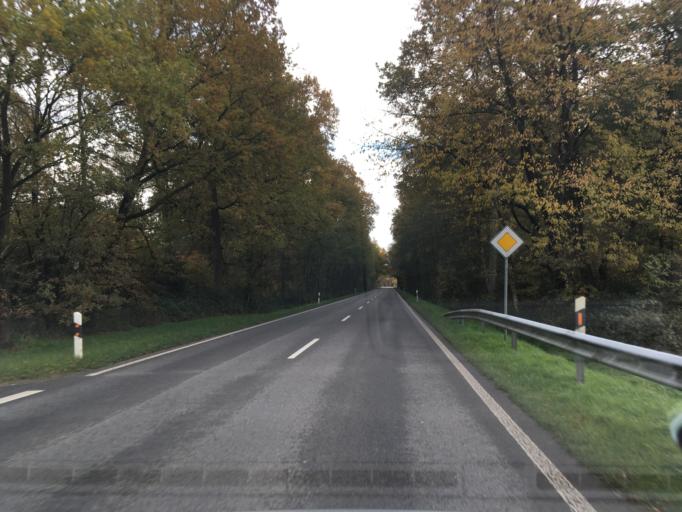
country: DE
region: North Rhine-Westphalia
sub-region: Regierungsbezirk Munster
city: Heiden
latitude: 51.8460
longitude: 6.9268
